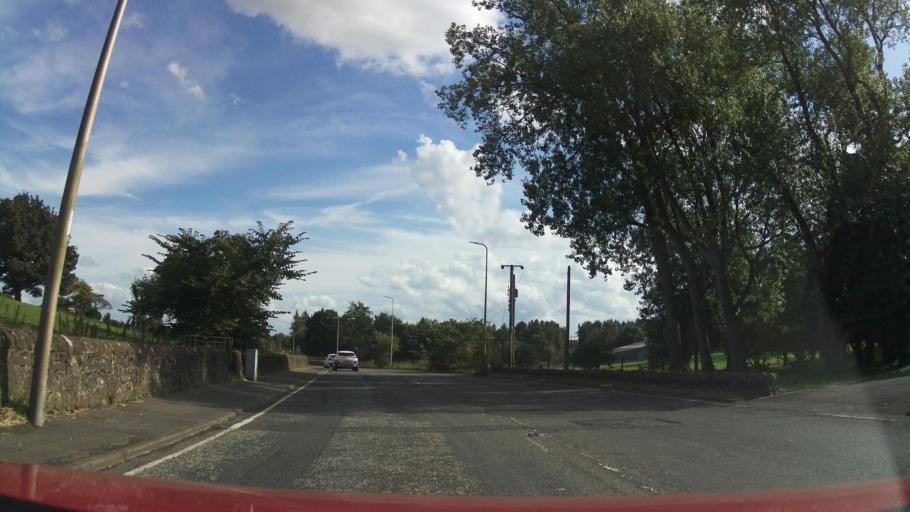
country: GB
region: Scotland
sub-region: Falkirk
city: Larbert
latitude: 56.0346
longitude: -3.8538
